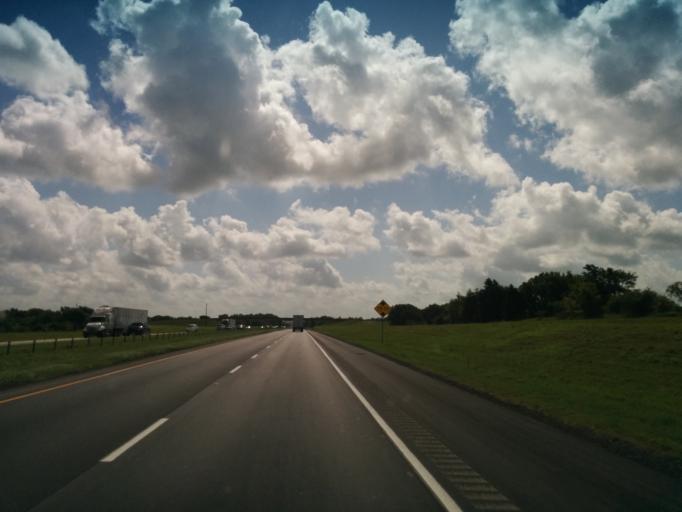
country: US
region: Texas
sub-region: Colorado County
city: Weimar
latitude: 29.6891
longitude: -96.8123
